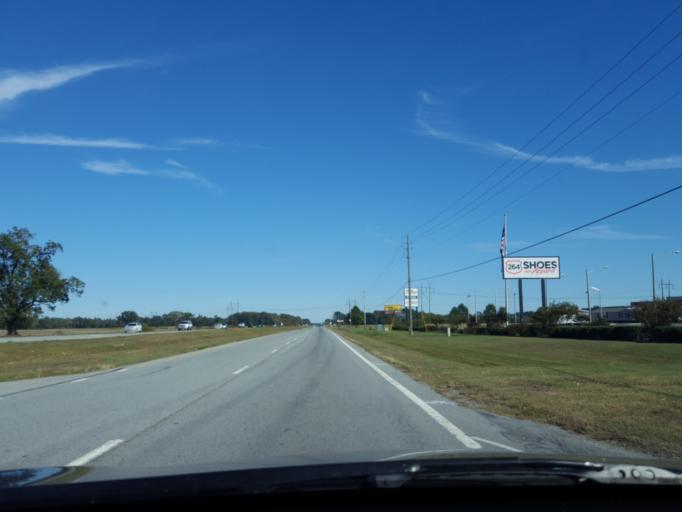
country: US
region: North Carolina
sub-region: Pitt County
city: Greenville
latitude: 35.6257
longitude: -77.3158
